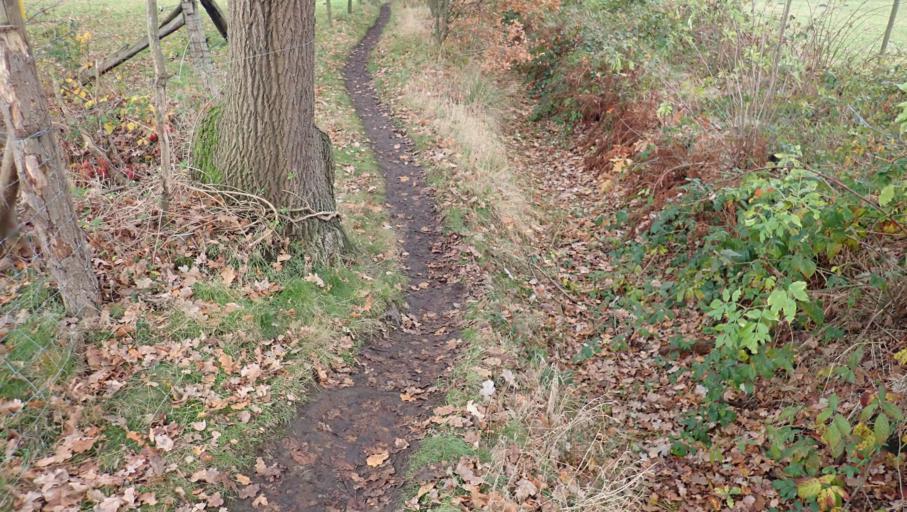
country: BE
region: Flanders
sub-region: Provincie Antwerpen
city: Hulshout
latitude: 51.0816
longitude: 4.7948
